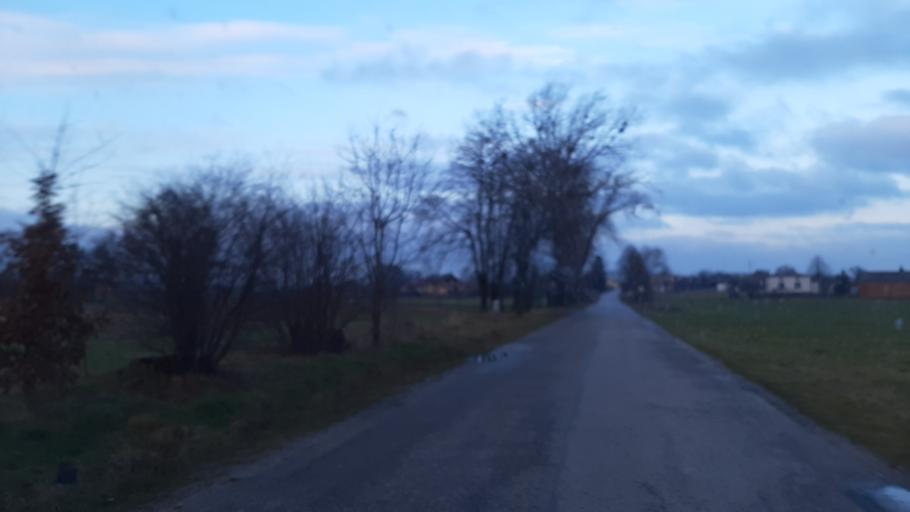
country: PL
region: Lublin Voivodeship
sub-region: Powiat lubartowski
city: Kamionka
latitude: 51.3989
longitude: 22.4113
